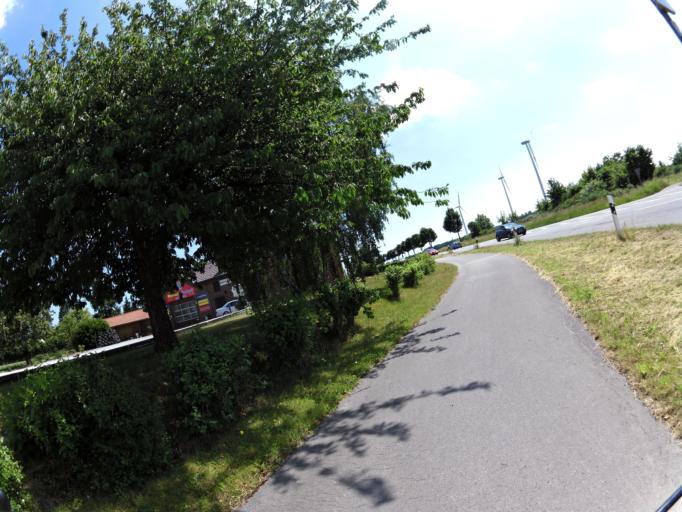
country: DE
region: North Rhine-Westphalia
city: Geilenkirchen
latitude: 51.0139
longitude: 6.1164
